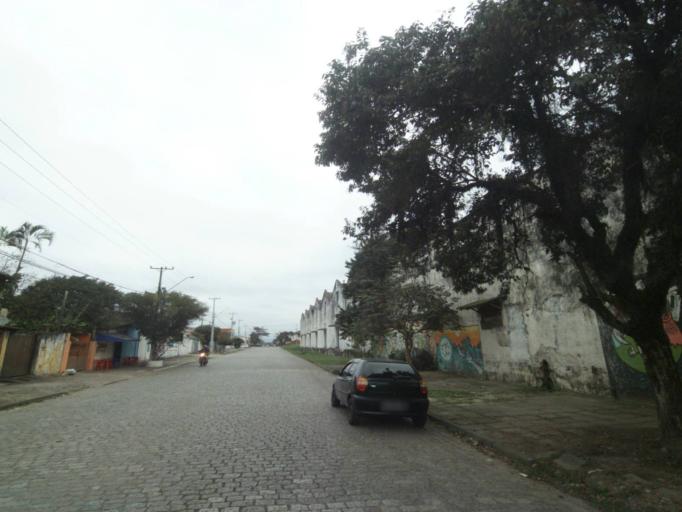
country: BR
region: Parana
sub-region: Paranagua
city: Paranagua
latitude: -25.5154
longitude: -48.5188
